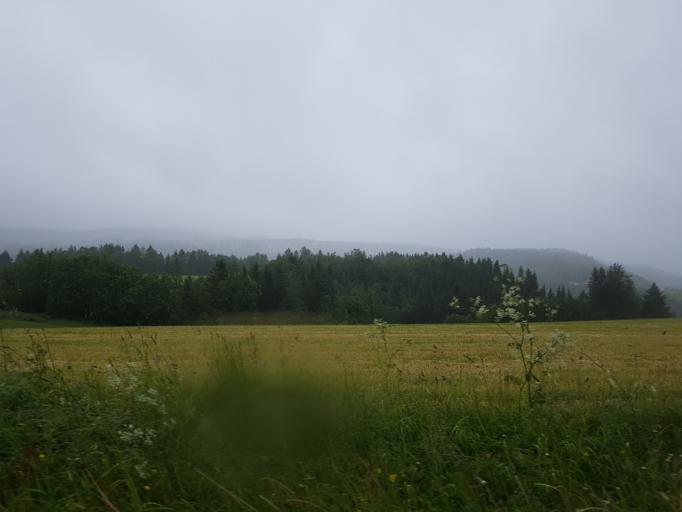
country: NO
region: Sor-Trondelag
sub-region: Selbu
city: Mebonden
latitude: 63.3820
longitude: 11.0823
